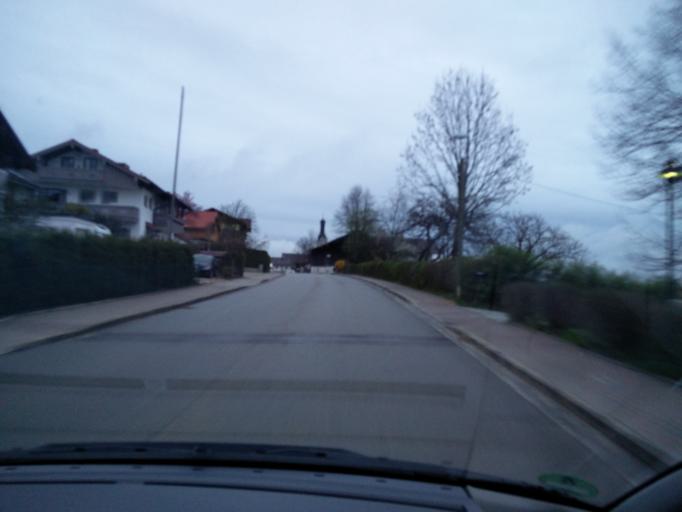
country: DE
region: Bavaria
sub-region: Upper Bavaria
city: Rimsting
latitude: 47.8757
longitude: 12.3375
